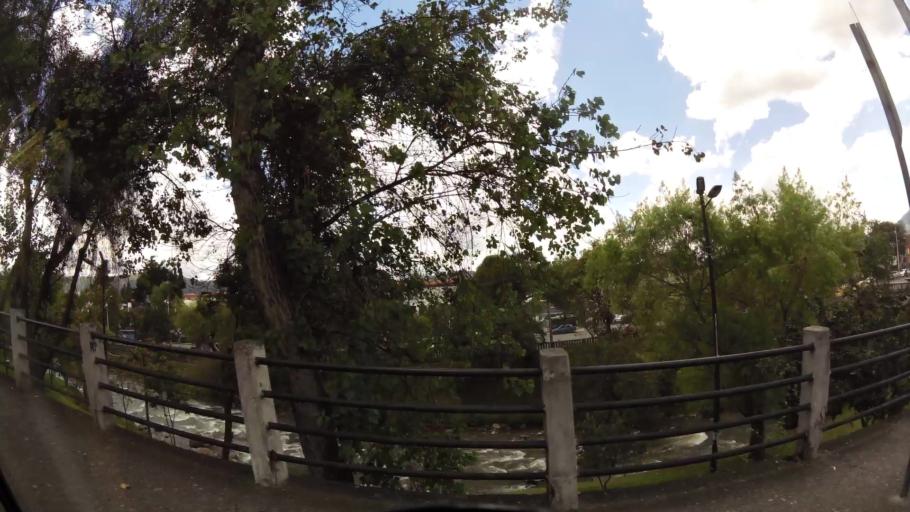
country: EC
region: Azuay
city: Cuenca
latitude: -2.8987
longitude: -79.0099
